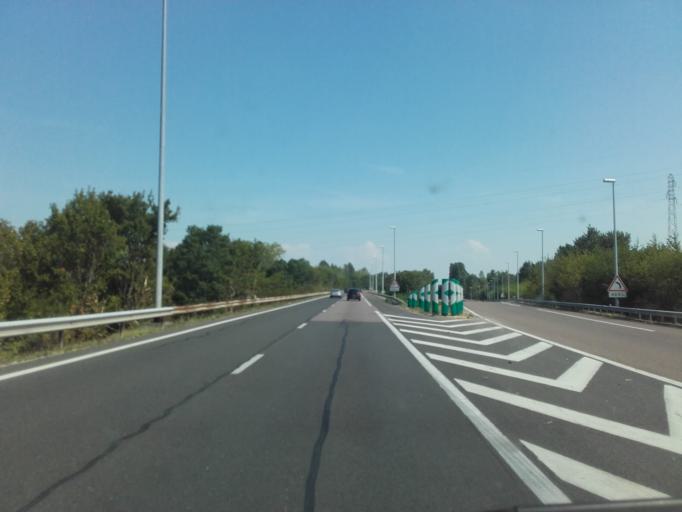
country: FR
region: Bourgogne
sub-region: Departement de la Cote-d'Or
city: Beaune
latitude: 47.0339
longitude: 4.8641
